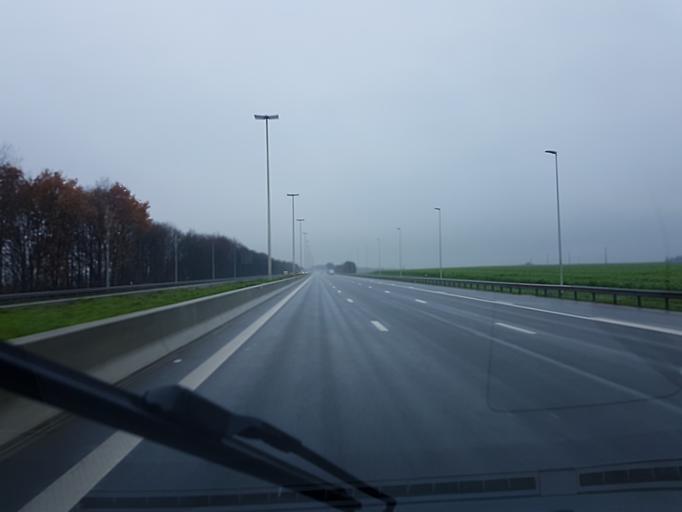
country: BE
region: Wallonia
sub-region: Province de Liege
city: Villers-le-Bouillet
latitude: 50.5901
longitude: 5.2584
